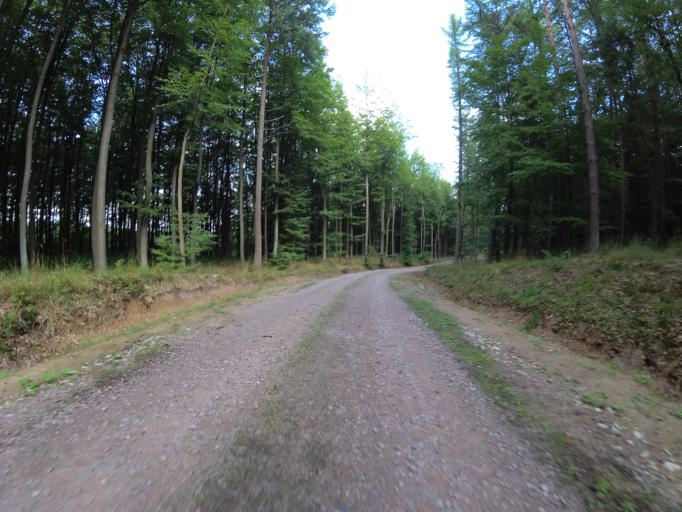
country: PL
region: Pomeranian Voivodeship
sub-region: Powiat wejherowski
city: Bojano
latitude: 54.5144
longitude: 18.4231
